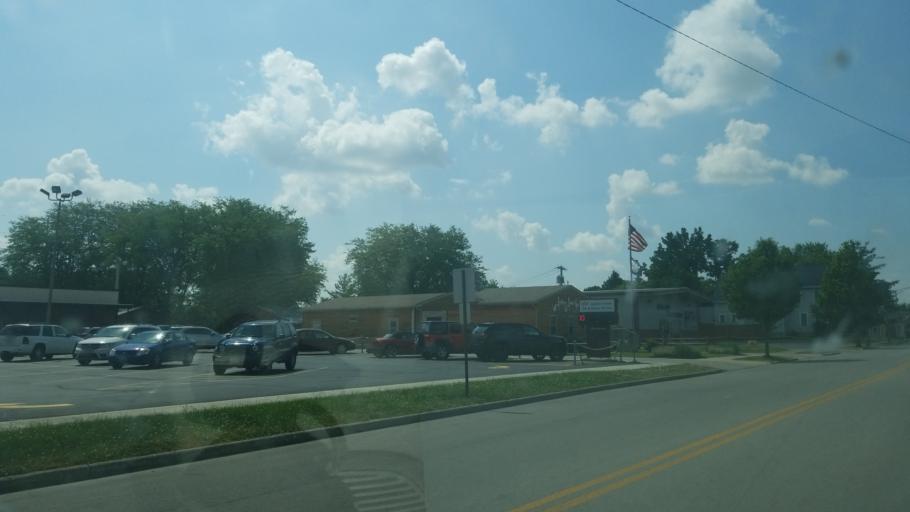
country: US
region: Ohio
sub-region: Auglaize County
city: Wapakoneta
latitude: 40.5713
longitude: -84.1838
